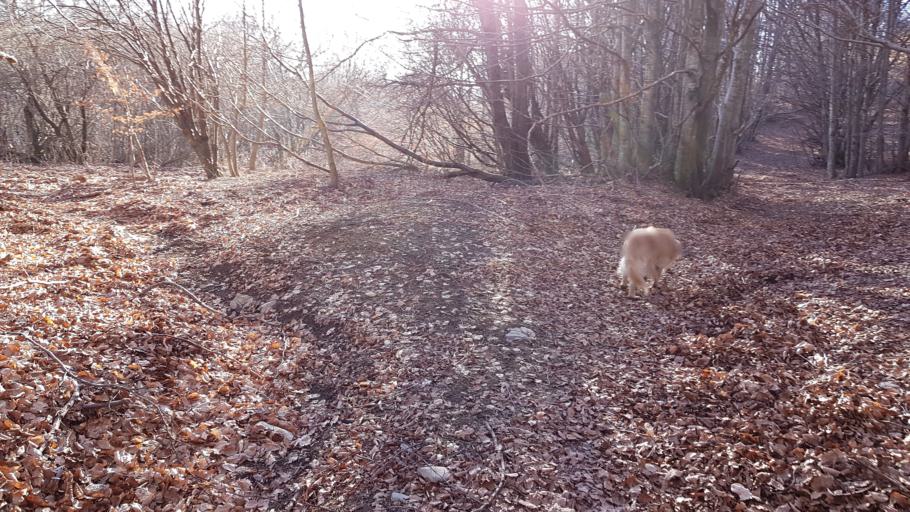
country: IT
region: Liguria
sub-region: Provincia di Genova
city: Torriglia
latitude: 44.5483
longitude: 9.1529
